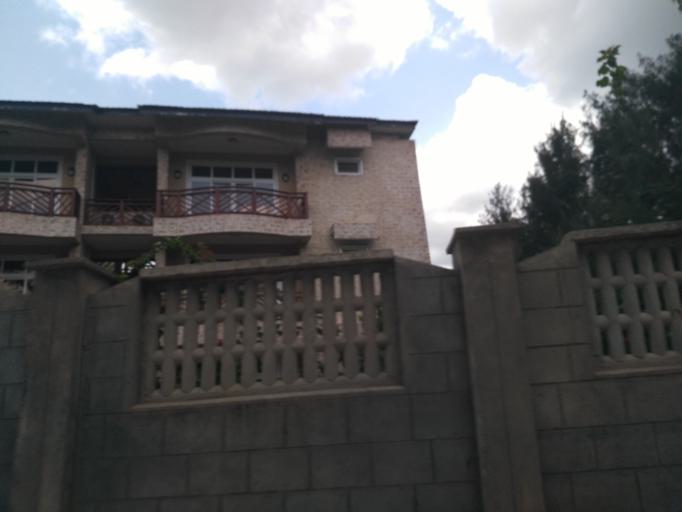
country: TZ
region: Dar es Salaam
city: Dar es Salaam
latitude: -6.8514
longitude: 39.3589
